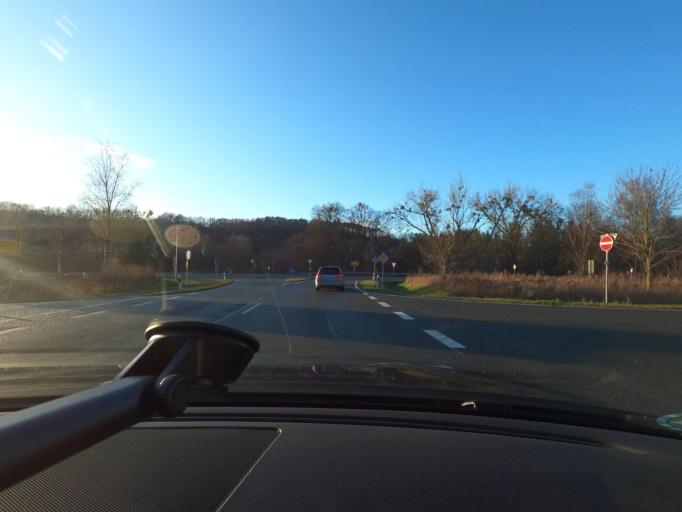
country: DE
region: Lower Saxony
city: Badenhausen
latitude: 51.7585
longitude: 10.2139
